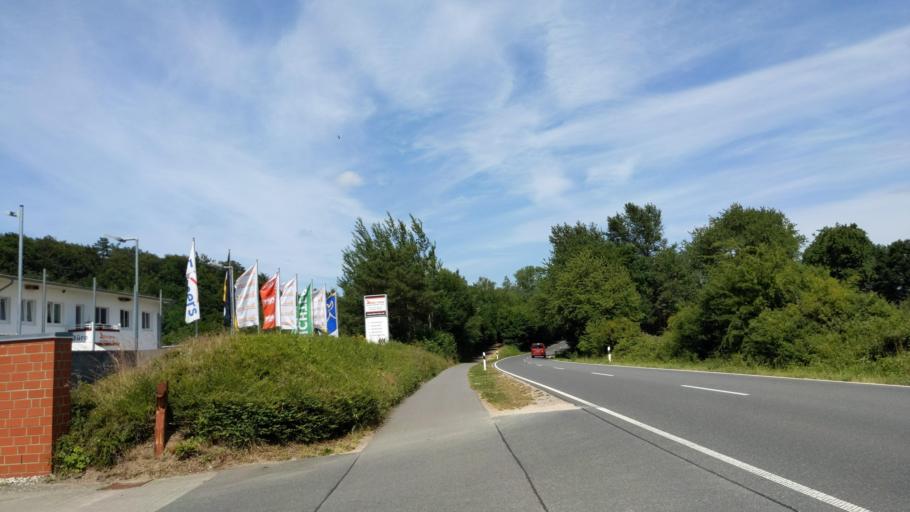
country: DE
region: Schleswig-Holstein
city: Malente
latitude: 54.1552
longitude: 10.5400
